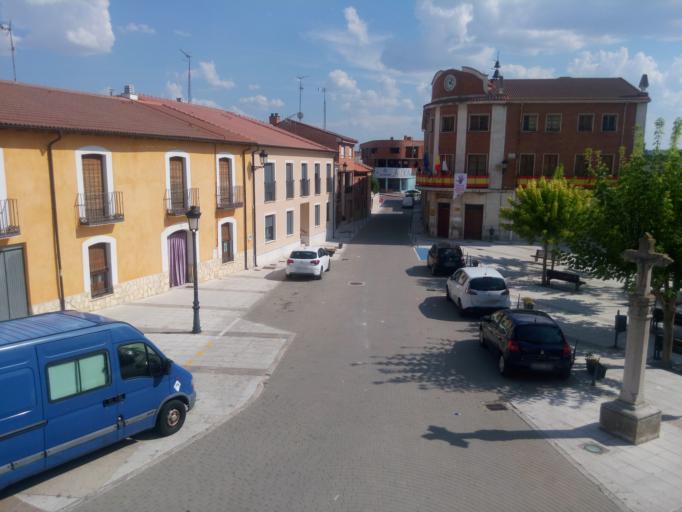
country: ES
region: Castille and Leon
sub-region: Provincia de Valladolid
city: Portillo
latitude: 41.4737
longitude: -4.5946
